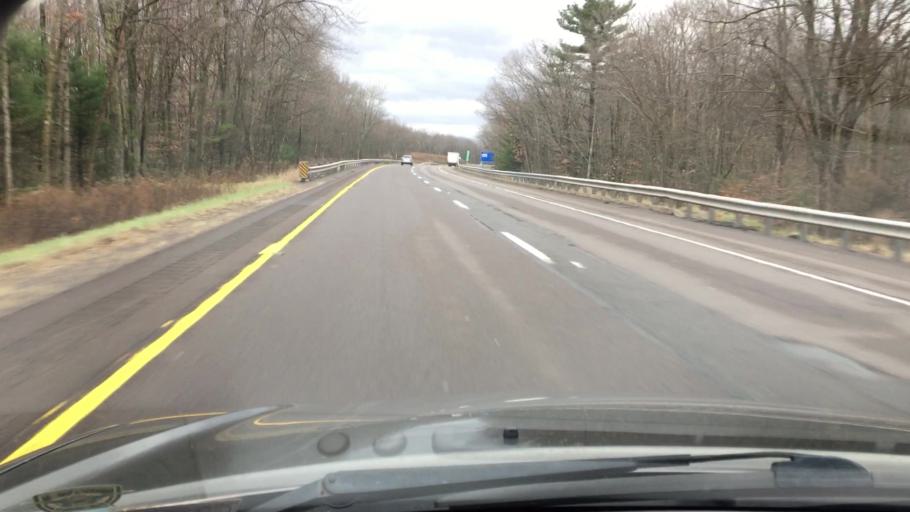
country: US
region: Pennsylvania
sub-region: Luzerne County
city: White Haven
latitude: 41.0715
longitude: -75.6850
